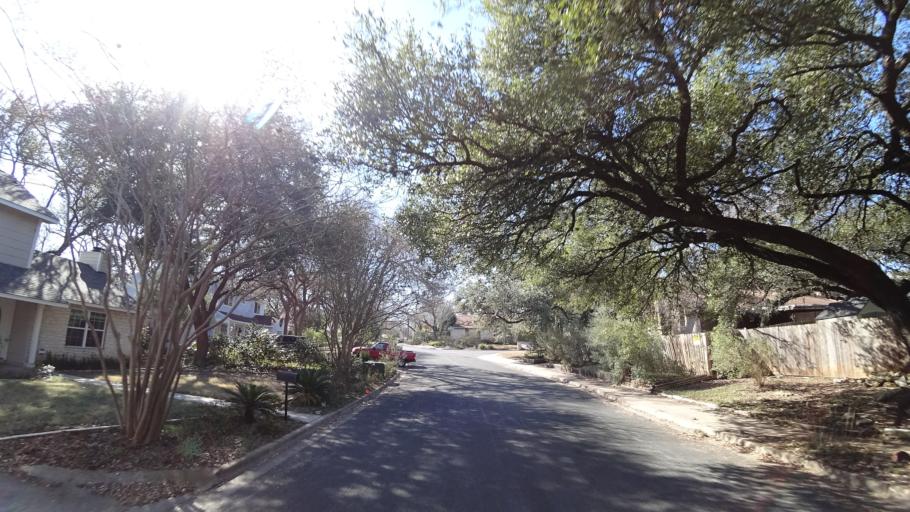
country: US
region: Texas
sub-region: Travis County
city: Wells Branch
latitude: 30.3887
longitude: -97.6864
